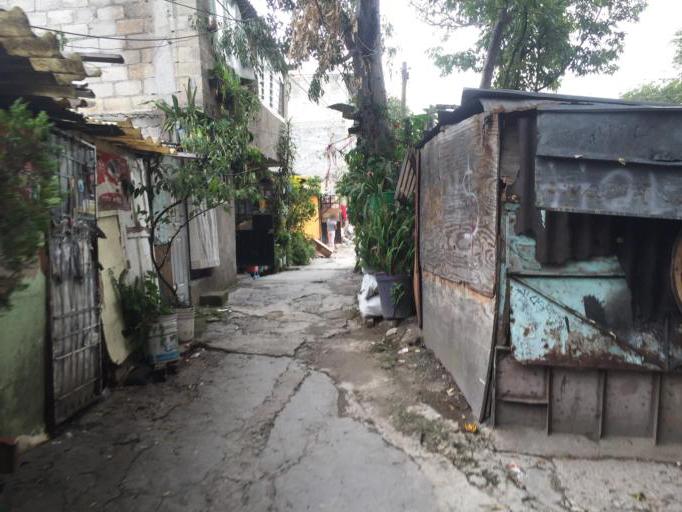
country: MX
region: Mexico City
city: Polanco
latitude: 19.3949
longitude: -99.1899
